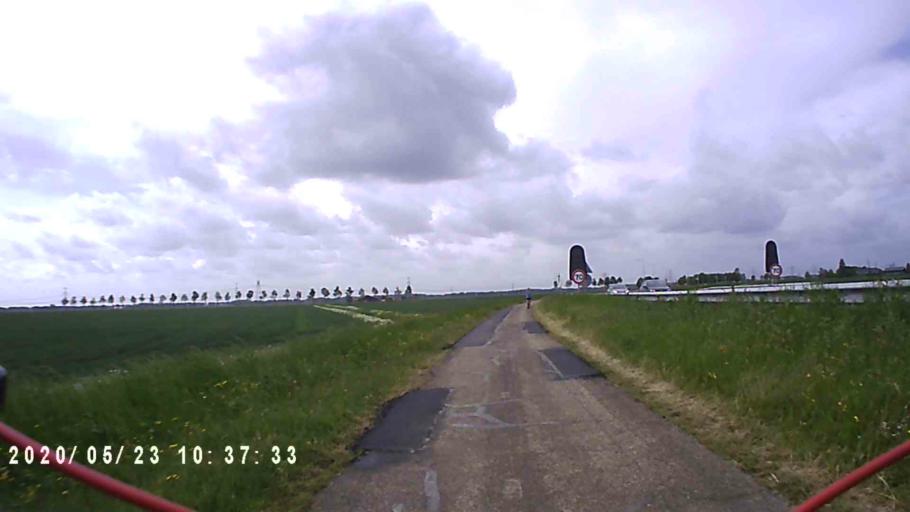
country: NL
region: Groningen
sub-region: Gemeente Appingedam
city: Appingedam
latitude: 53.3065
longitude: 6.8837
